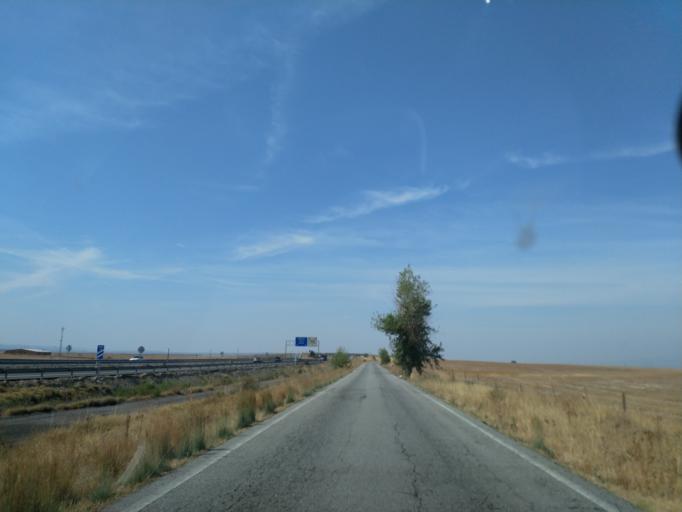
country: ES
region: Extremadura
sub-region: Provincia de Caceres
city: Berrocalejo
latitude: 39.8954
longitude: -5.3381
